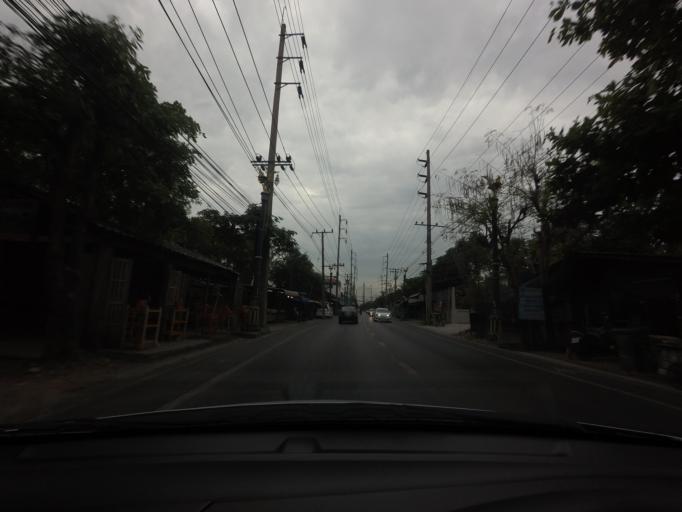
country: TH
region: Samut Prakan
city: Phra Pradaeng
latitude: 13.6686
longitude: 100.5536
